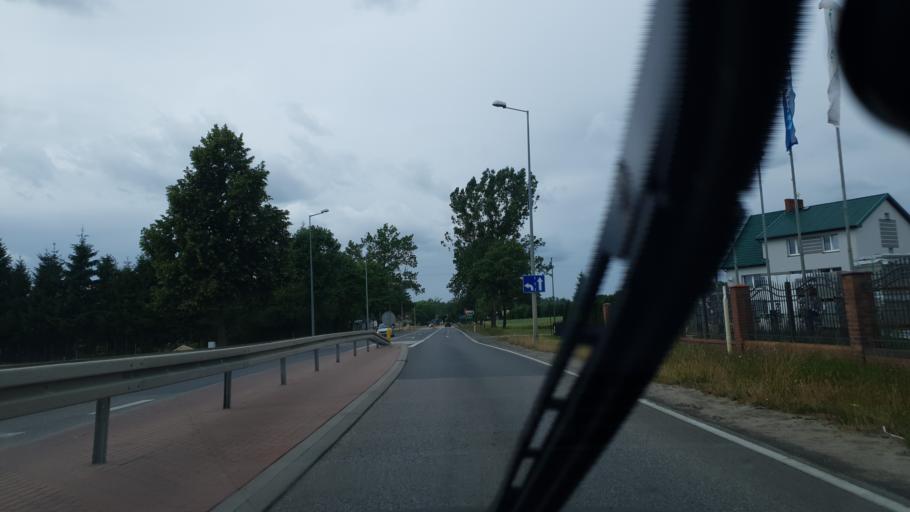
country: PL
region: Pomeranian Voivodeship
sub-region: Powiat kartuski
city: Banino
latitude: 54.3899
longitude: 18.3593
